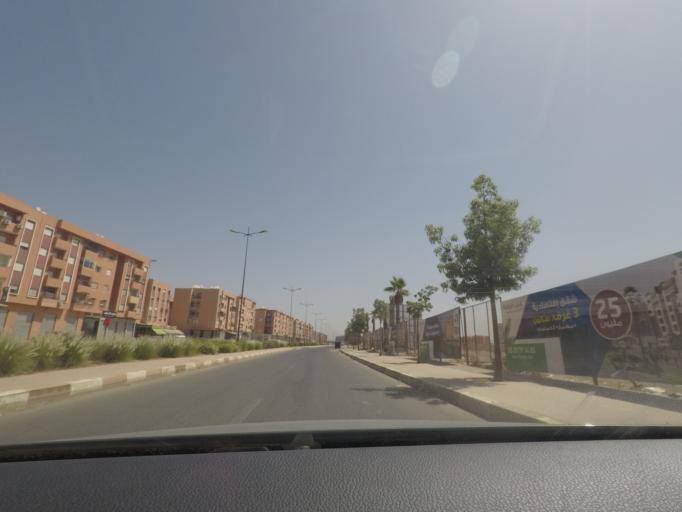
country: MA
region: Marrakech-Tensift-Al Haouz
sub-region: Marrakech
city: Marrakesh
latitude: 31.5867
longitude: -8.0416
